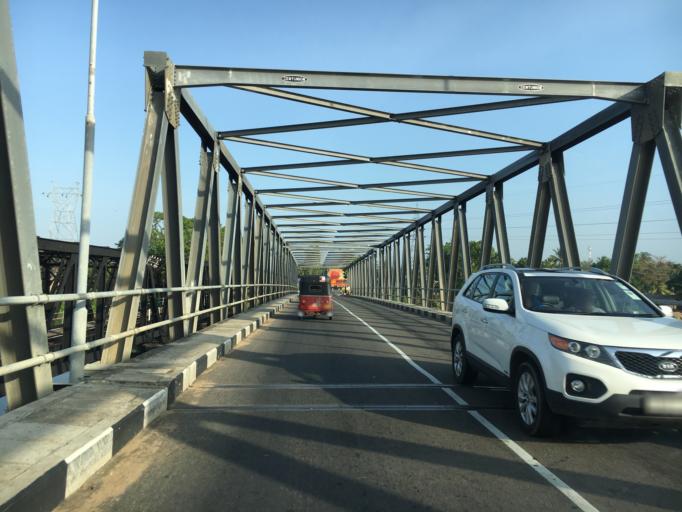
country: LK
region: Eastern Province
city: Eravur Town
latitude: 7.9216
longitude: 81.5150
